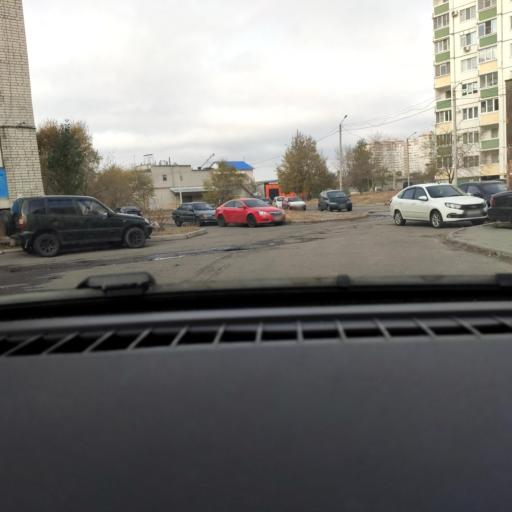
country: RU
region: Voronezj
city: Maslovka
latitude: 51.5900
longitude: 39.2448
